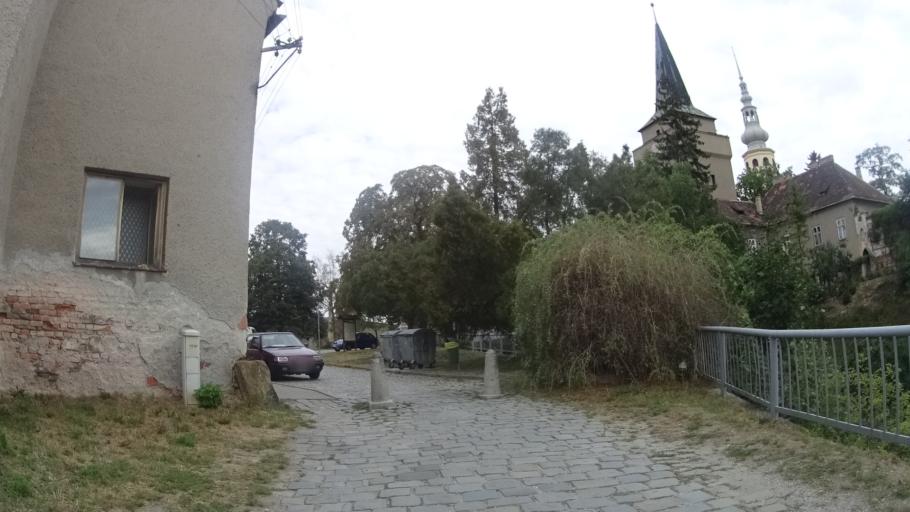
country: CZ
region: Olomoucky
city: Tovacov
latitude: 49.4291
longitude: 17.2897
